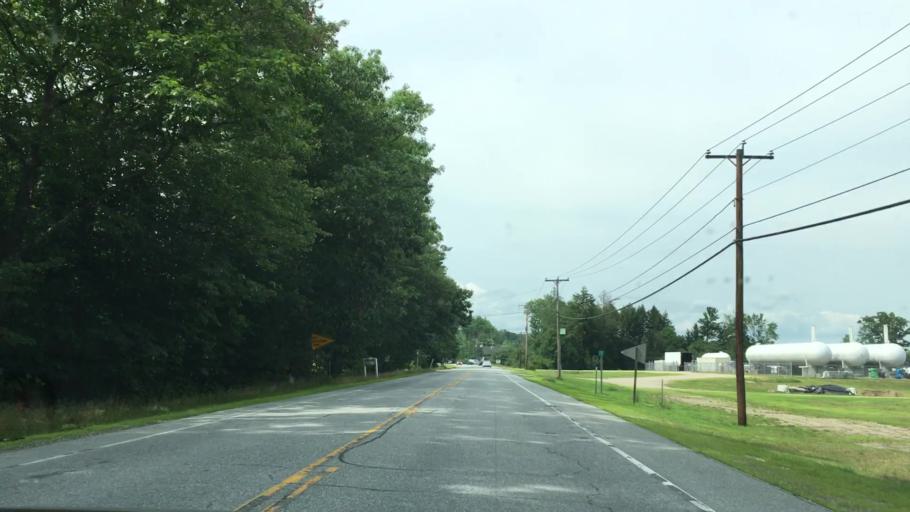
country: US
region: New Hampshire
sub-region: Hillsborough County
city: Antrim
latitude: 43.0167
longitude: -71.9337
